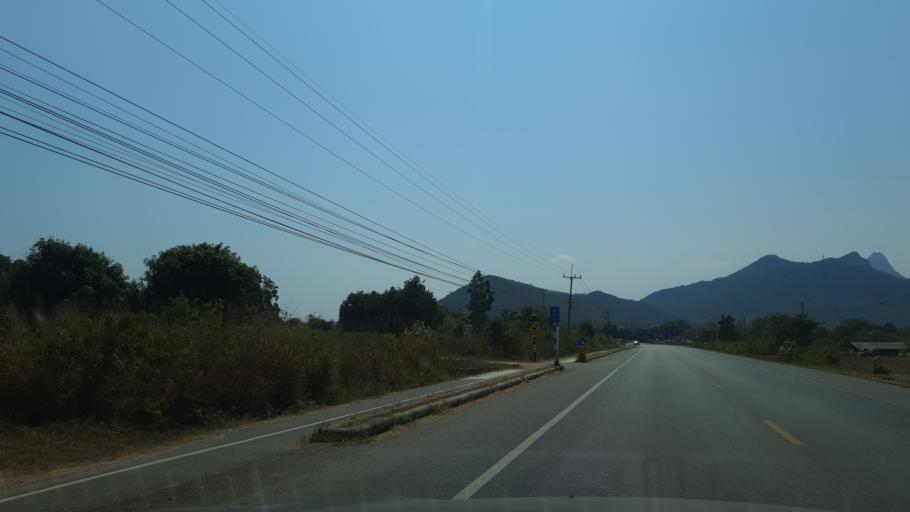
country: TH
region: Prachuap Khiri Khan
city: Sam Roi Yot
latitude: 12.3030
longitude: 99.9600
